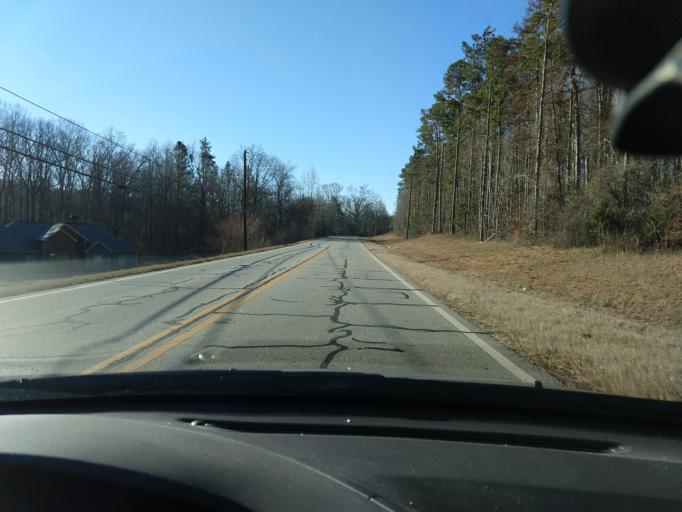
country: US
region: Georgia
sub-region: Jackson County
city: Commerce
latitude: 34.1763
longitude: -83.4872
